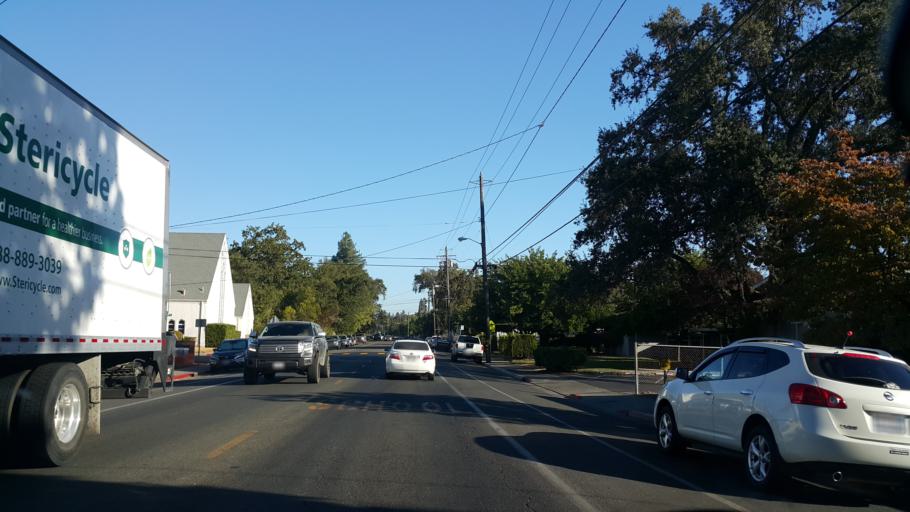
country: US
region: California
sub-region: Mendocino County
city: Ukiah
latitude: 39.1383
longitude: -123.2099
